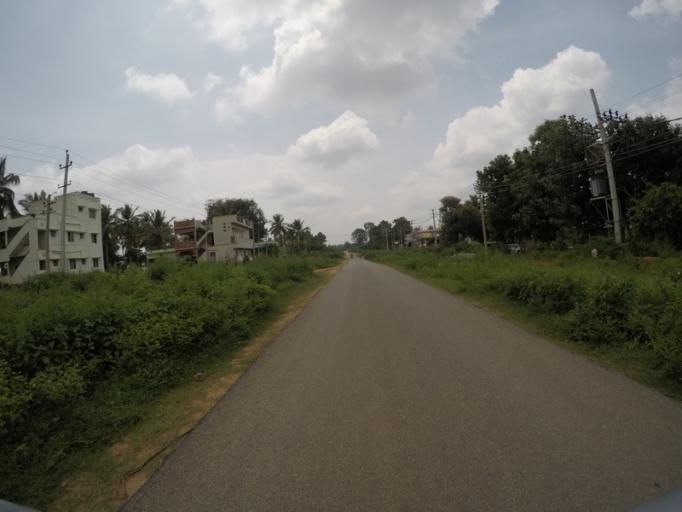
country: IN
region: Karnataka
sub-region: Ramanagara
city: Kanakapura
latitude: 12.6880
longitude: 77.4640
